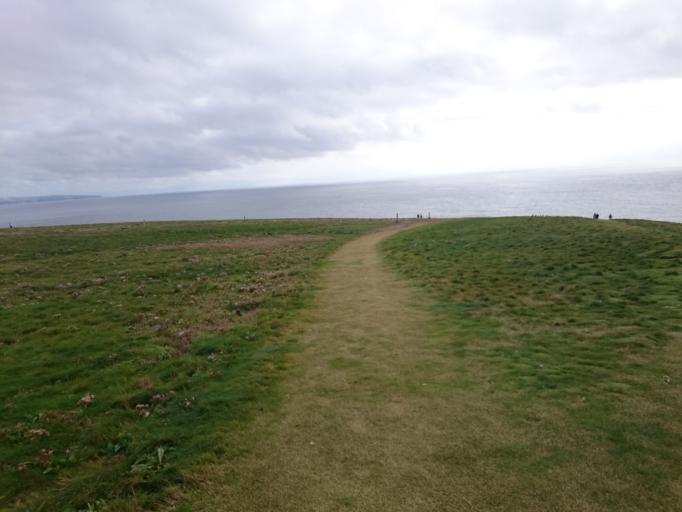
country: IE
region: Munster
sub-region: Ciarrai
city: Ballybunnion
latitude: 52.5604
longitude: -9.9367
